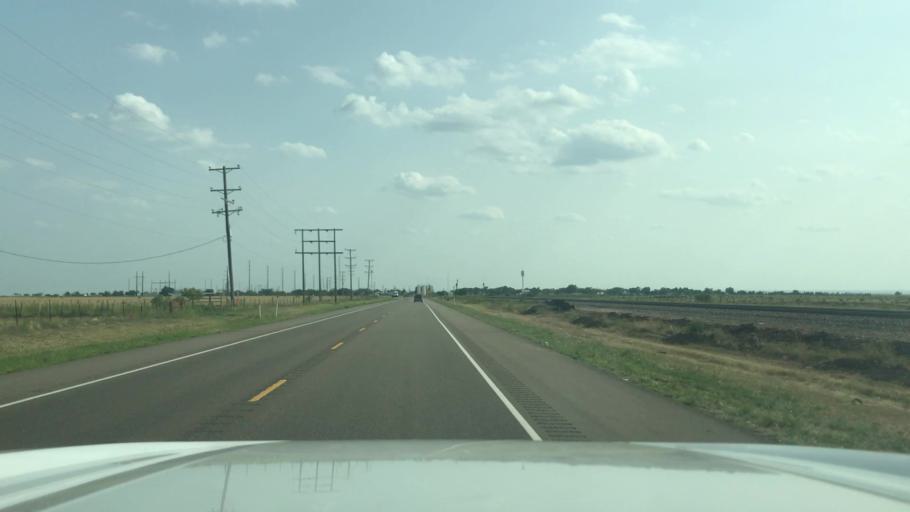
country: US
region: Texas
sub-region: Hartley County
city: Channing
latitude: 35.6990
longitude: -102.3270
